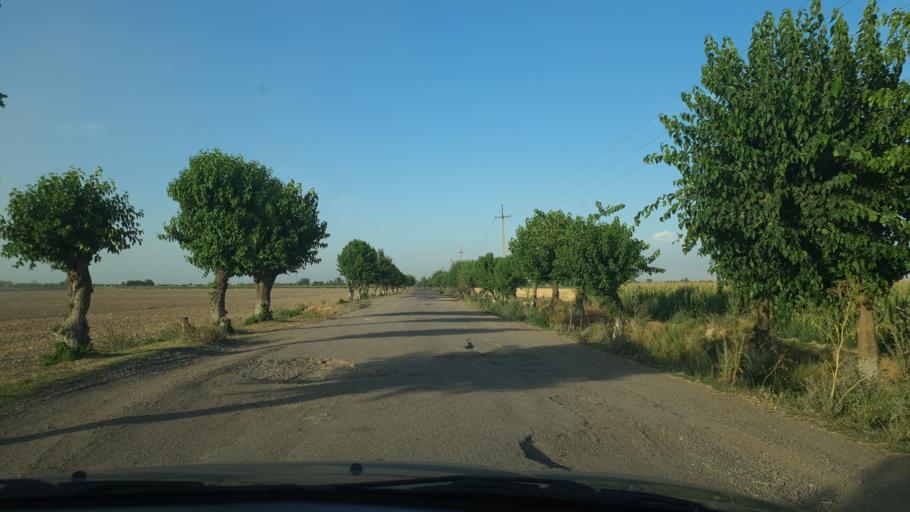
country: UZ
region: Toshkent
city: Tuytepa
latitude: 41.0977
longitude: 69.3761
